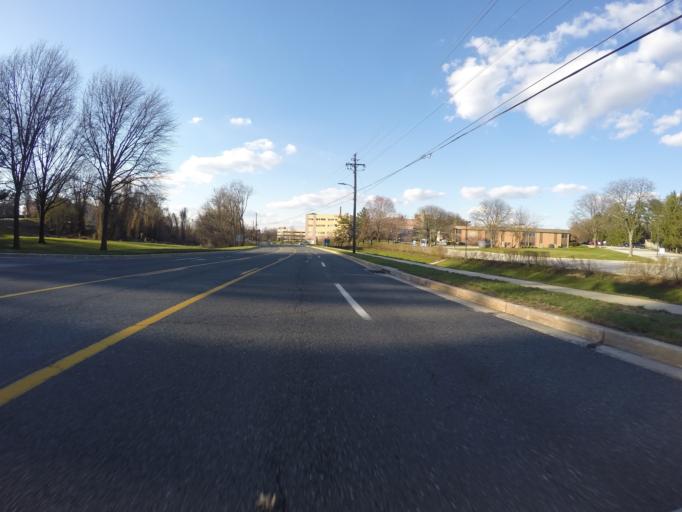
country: US
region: Maryland
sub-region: Baltimore County
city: Towson
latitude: 39.3838
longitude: -76.6112
